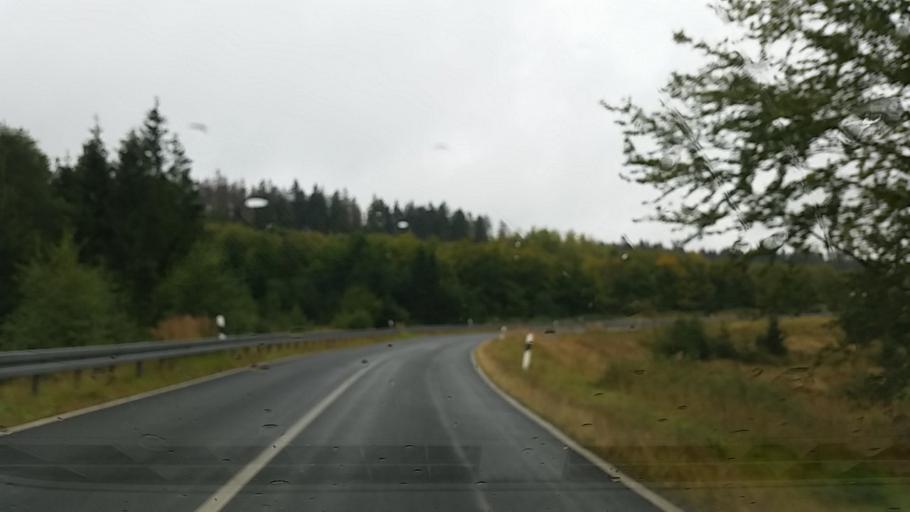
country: DE
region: Lower Saxony
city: Altenau
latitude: 51.7809
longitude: 10.4362
